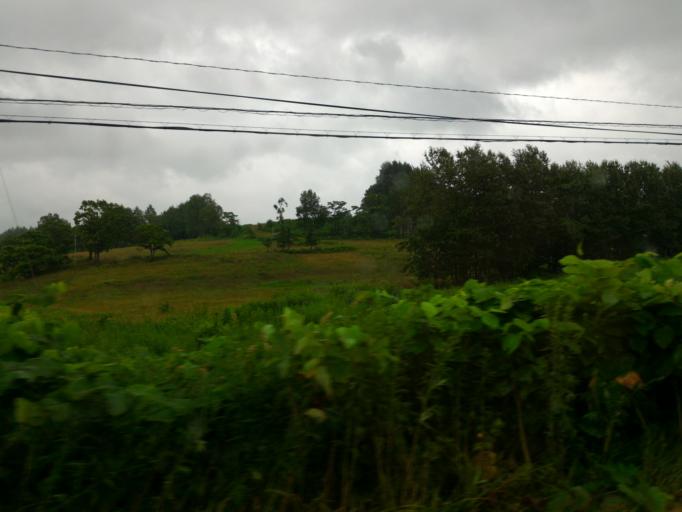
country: JP
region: Hokkaido
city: Nayoro
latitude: 44.6686
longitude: 142.2688
